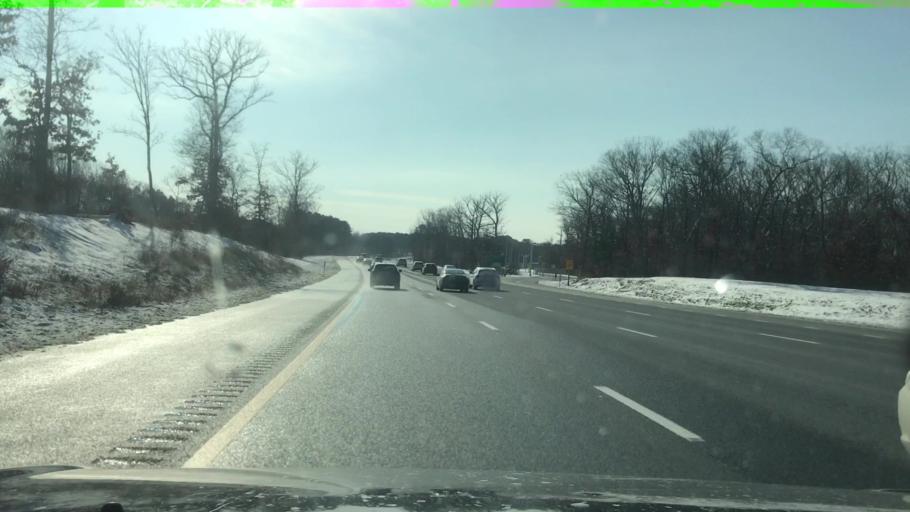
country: US
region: New Jersey
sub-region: Monmouth County
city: Ramtown
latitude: 40.1249
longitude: -74.1267
